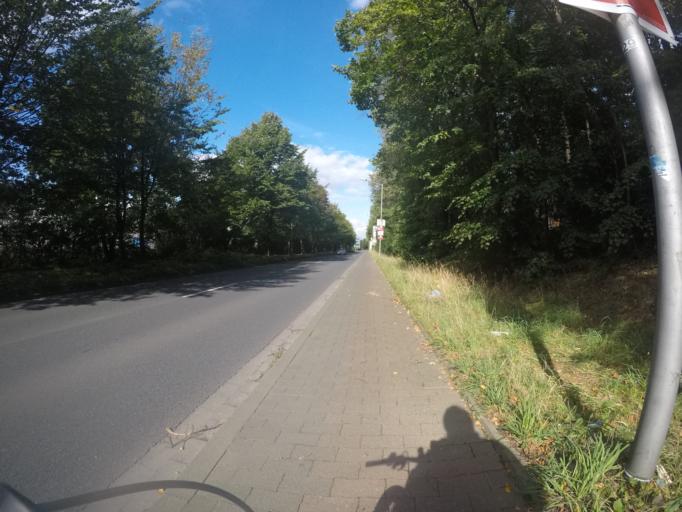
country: DE
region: North Rhine-Westphalia
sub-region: Regierungsbezirk Detmold
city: Herford
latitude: 52.1260
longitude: 8.6657
